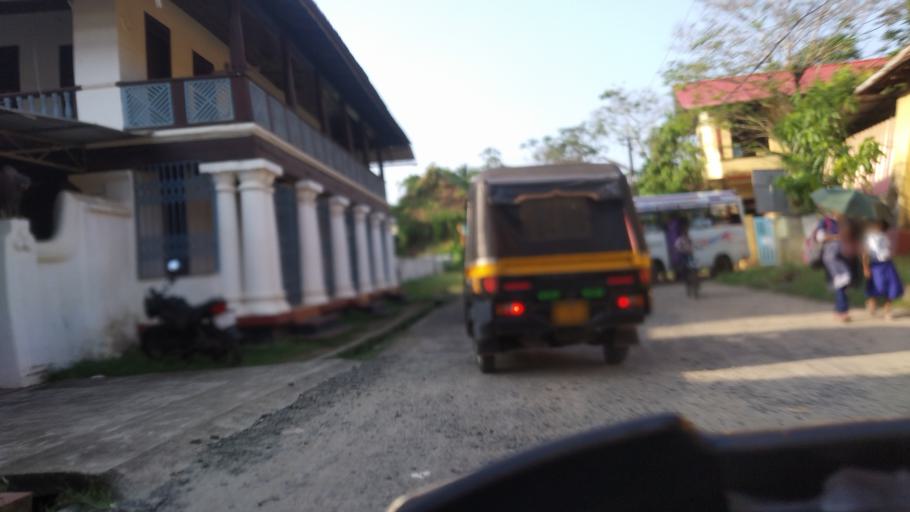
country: IN
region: Kerala
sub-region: Ernakulam
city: Elur
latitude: 10.0478
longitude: 76.2199
